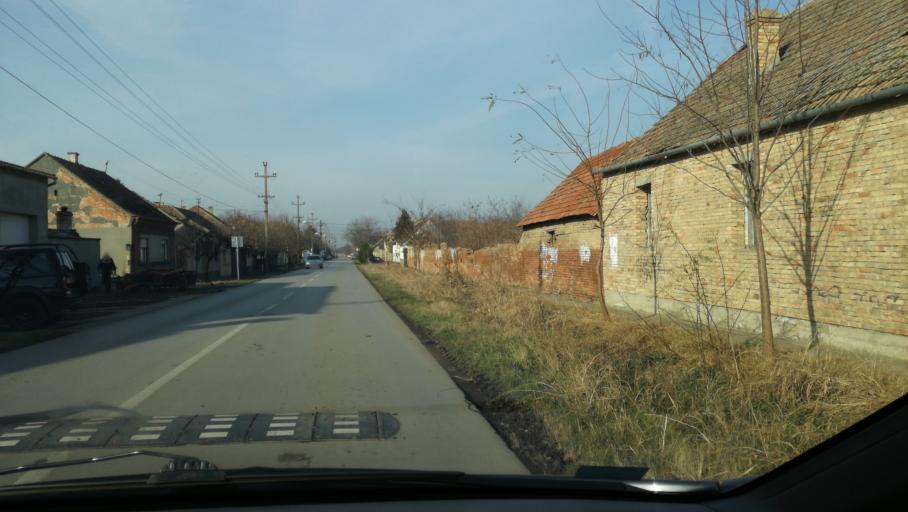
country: RS
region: Autonomna Pokrajina Vojvodina
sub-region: Severnobanatski Okrug
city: Kikinda
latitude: 45.8386
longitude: 20.4741
